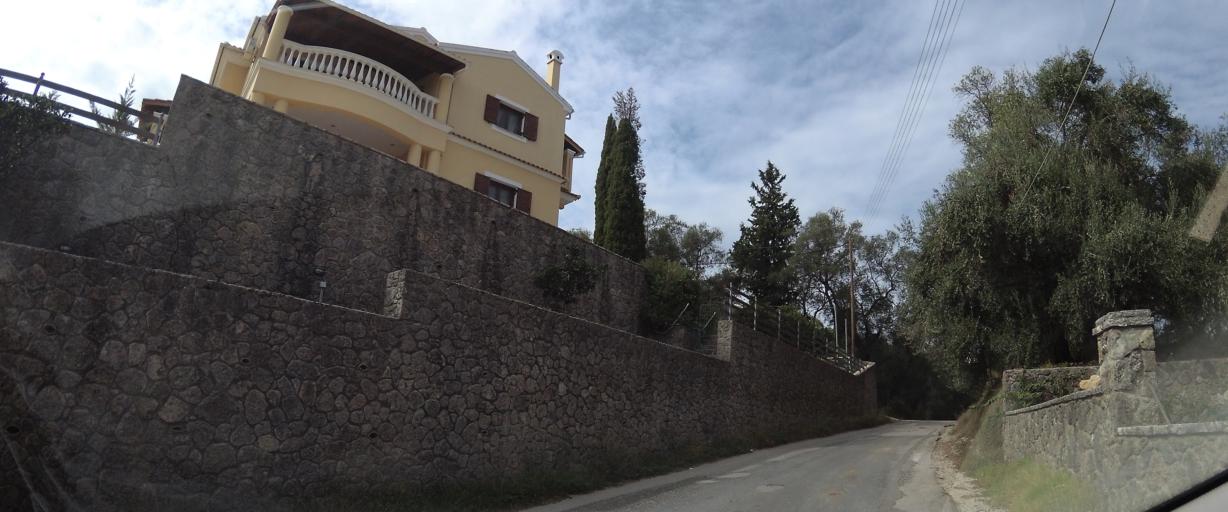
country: GR
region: Ionian Islands
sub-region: Nomos Kerkyras
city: Kontokali
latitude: 39.6900
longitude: 19.8165
